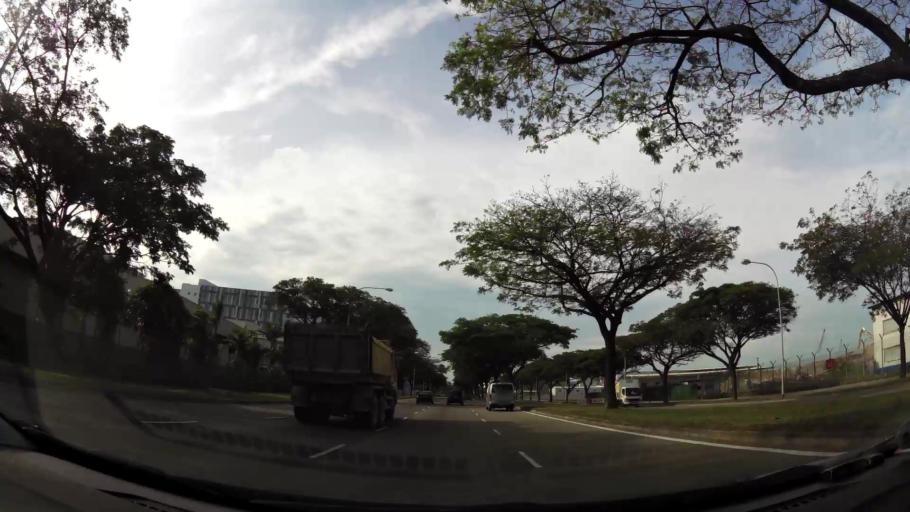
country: MY
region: Johor
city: Johor Bahru
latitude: 1.3061
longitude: 103.6258
